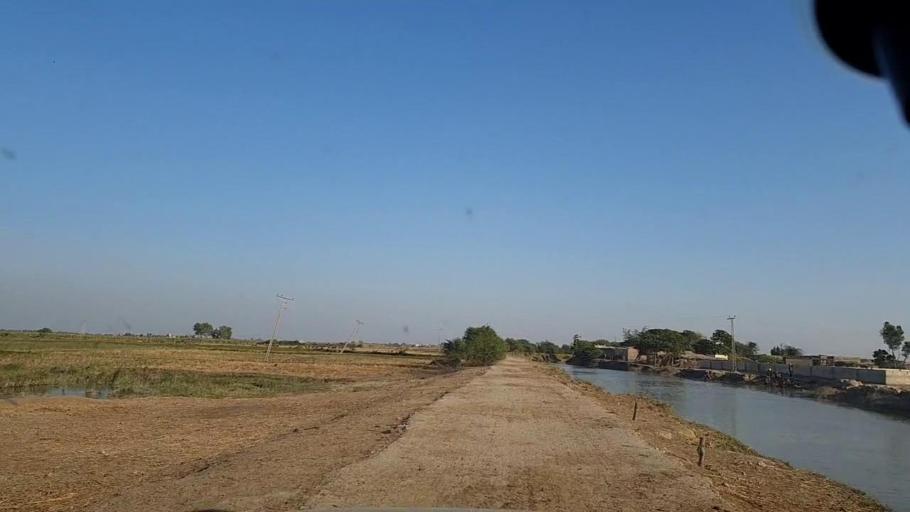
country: PK
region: Sindh
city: Chuhar Jamali
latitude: 24.5636
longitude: 68.0664
